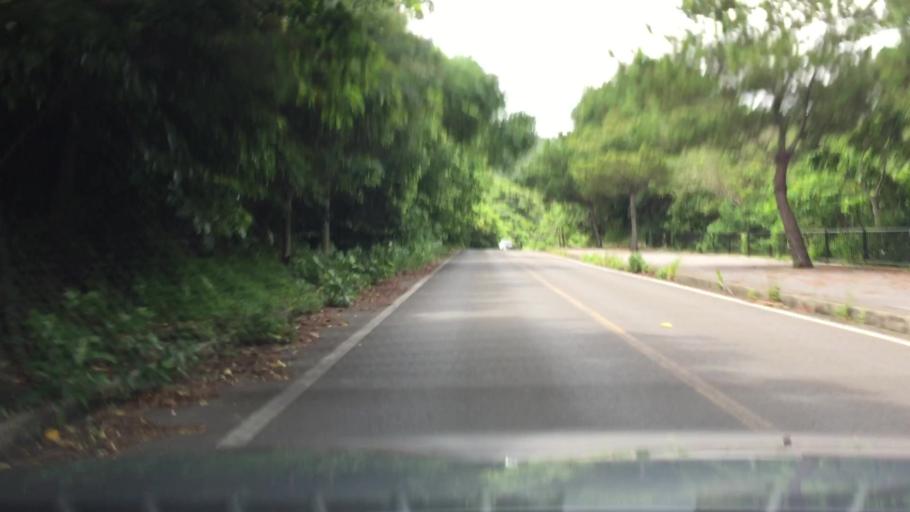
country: JP
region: Okinawa
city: Ishigaki
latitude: 24.4261
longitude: 124.2115
